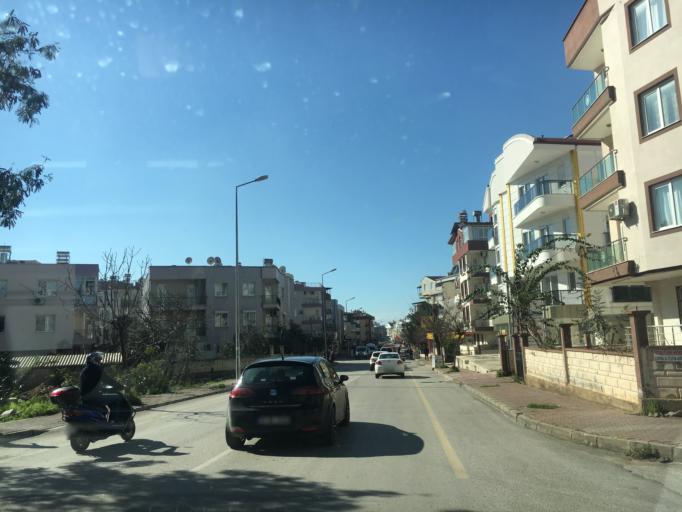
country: TR
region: Antalya
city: Antalya
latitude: 36.9167
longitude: 30.7071
